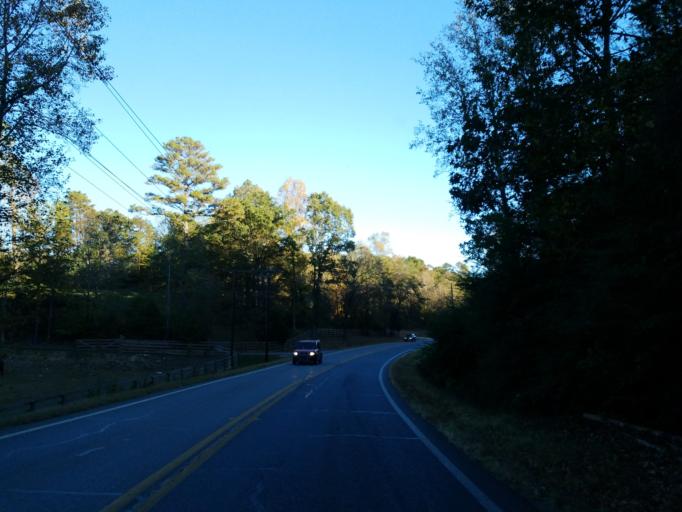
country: US
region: Georgia
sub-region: Dawson County
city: Dawsonville
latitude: 34.4265
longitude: -84.1546
